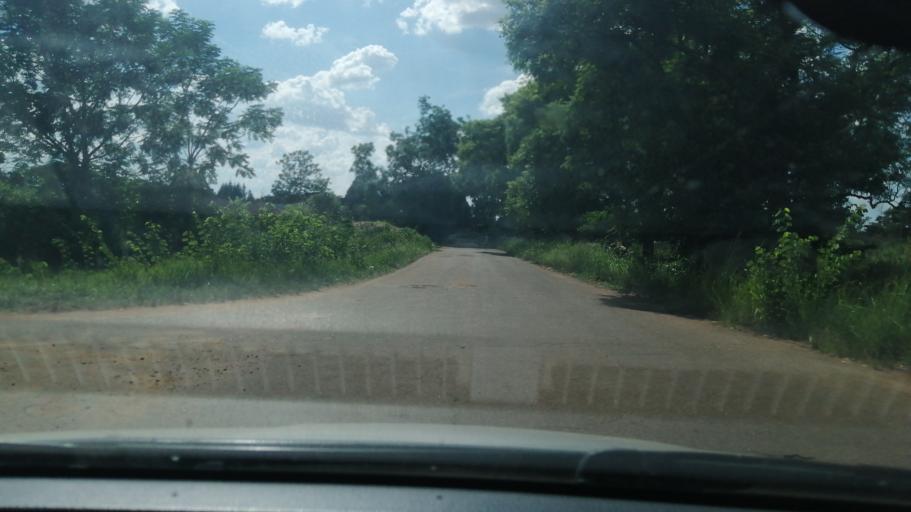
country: ZW
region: Harare
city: Harare
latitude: -17.7558
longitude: 31.0723
